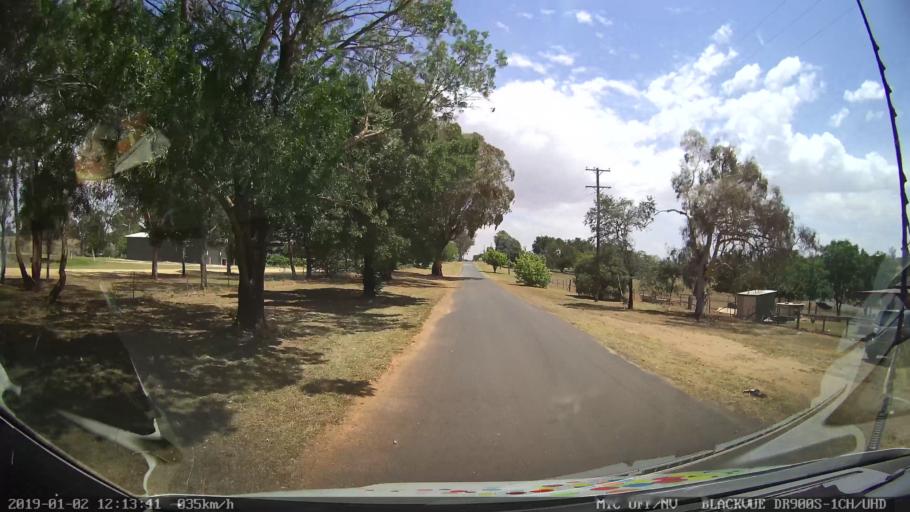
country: AU
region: New South Wales
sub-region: Young
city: Young
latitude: -34.4286
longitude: 148.2467
